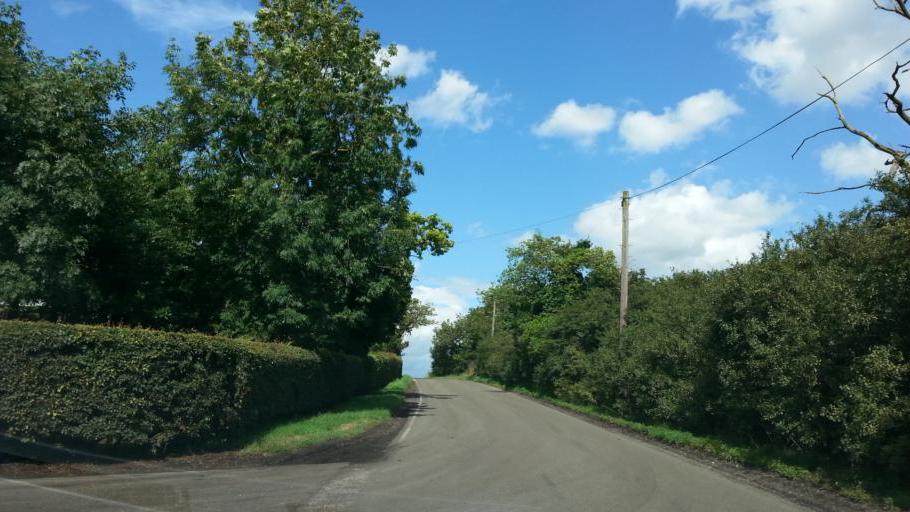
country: GB
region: England
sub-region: Nottinghamshire
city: Southwell
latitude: 53.1143
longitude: -0.9060
